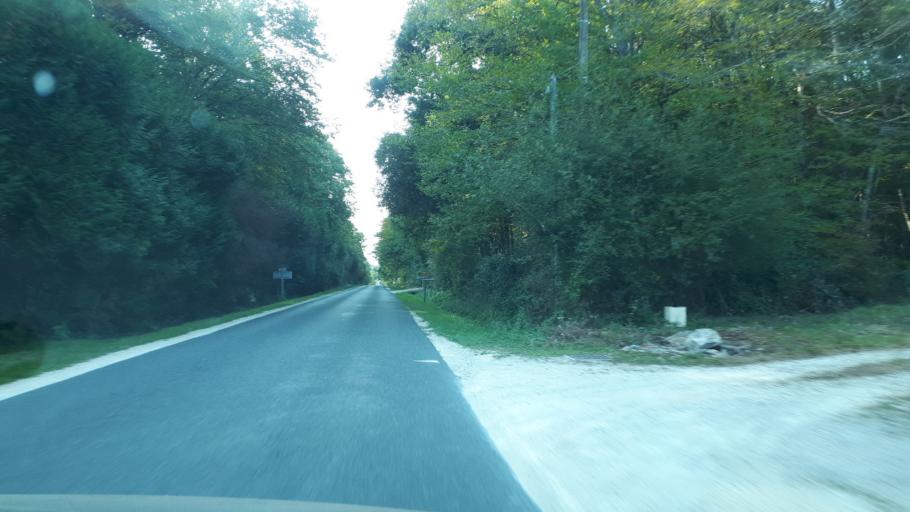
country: FR
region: Centre
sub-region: Departement du Cher
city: Saint-Eloy-de-Gy
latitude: 47.2260
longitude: 2.3092
